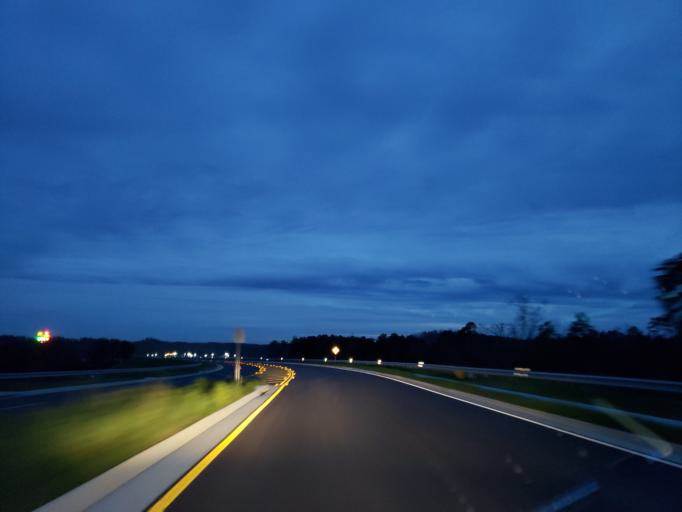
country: US
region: Georgia
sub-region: Bartow County
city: Emerson
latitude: 34.1260
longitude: -84.7418
